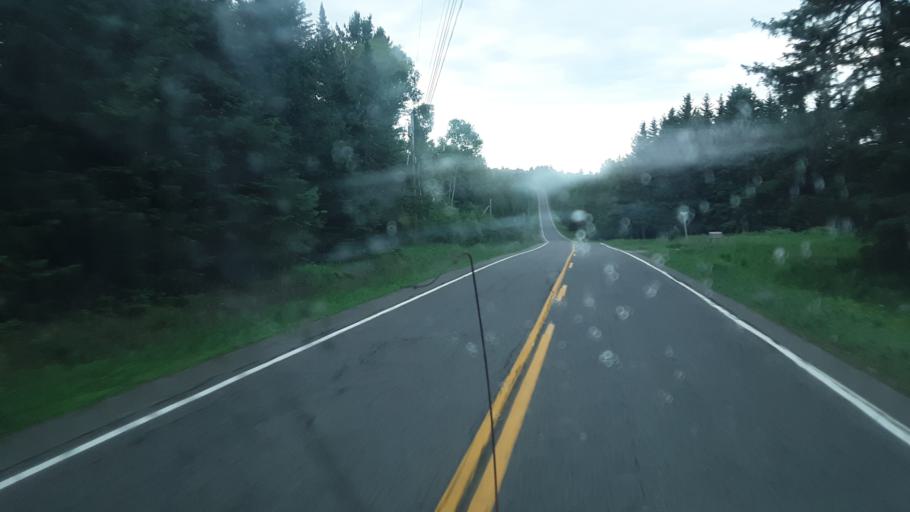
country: US
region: Maine
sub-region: Aroostook County
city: Presque Isle
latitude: 46.4759
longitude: -68.3881
